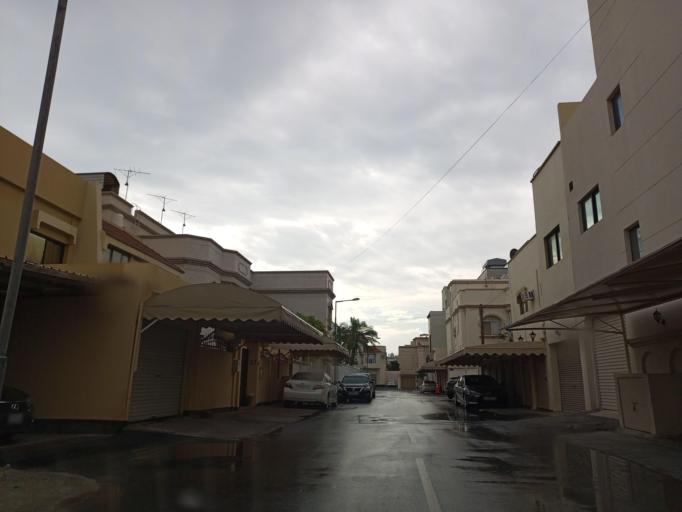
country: BH
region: Muharraq
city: Al Hadd
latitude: 26.2544
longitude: 50.6469
